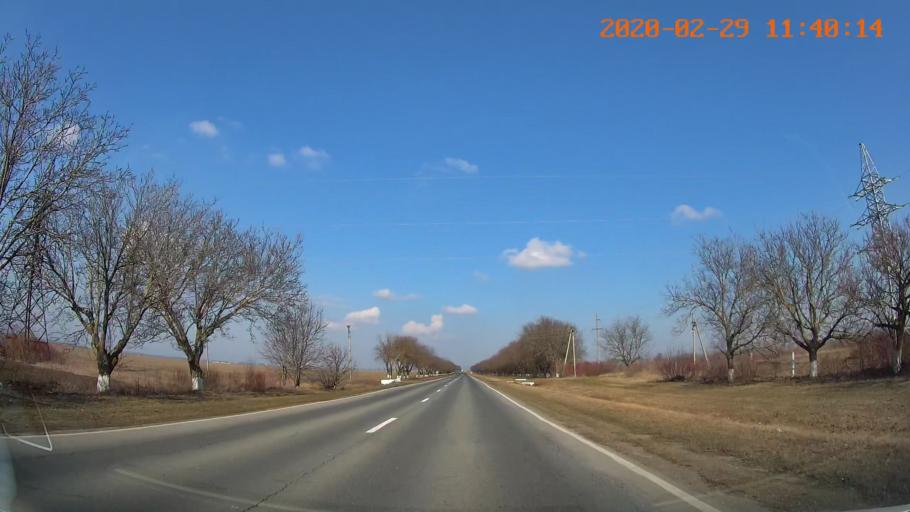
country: MD
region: Rezina
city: Saharna
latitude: 47.6531
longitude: 29.0210
